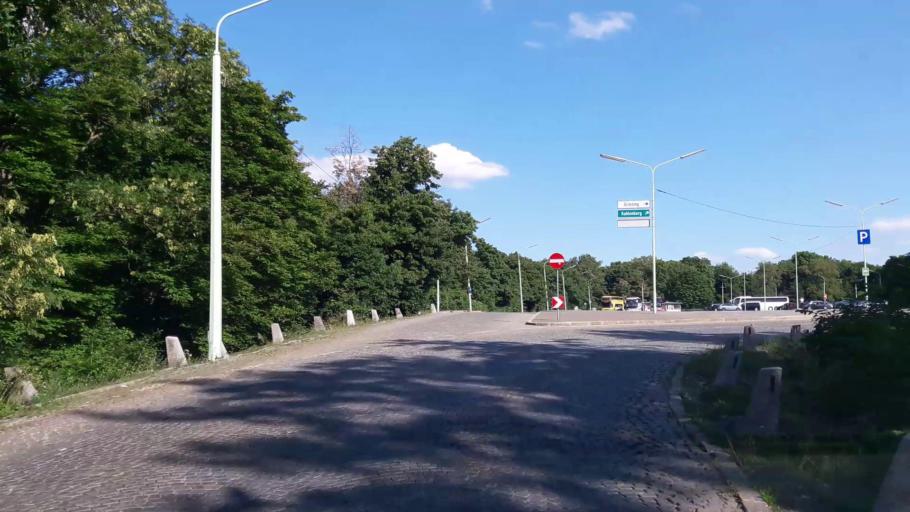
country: AT
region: Lower Austria
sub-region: Politischer Bezirk Korneuburg
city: Langenzersdorf
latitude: 48.2776
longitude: 16.3348
